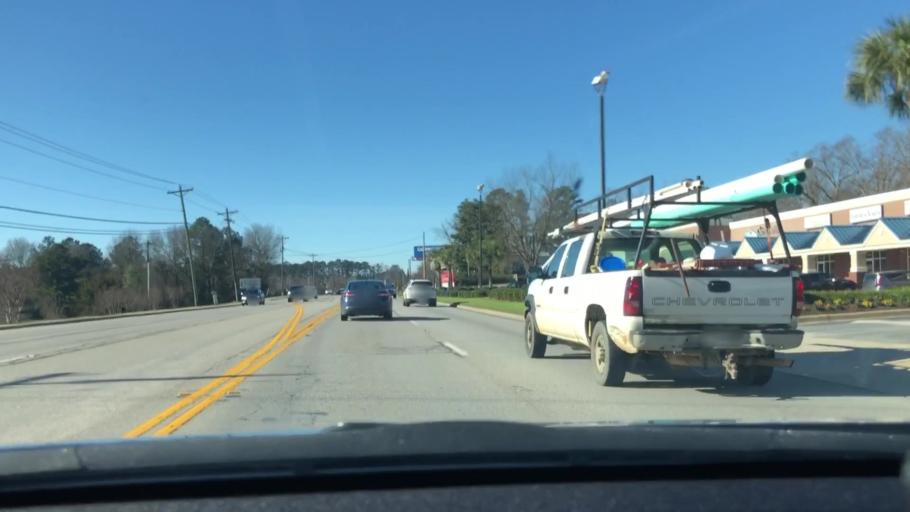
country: US
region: South Carolina
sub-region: Lexington County
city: Lexington
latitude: 34.0073
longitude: -81.1970
